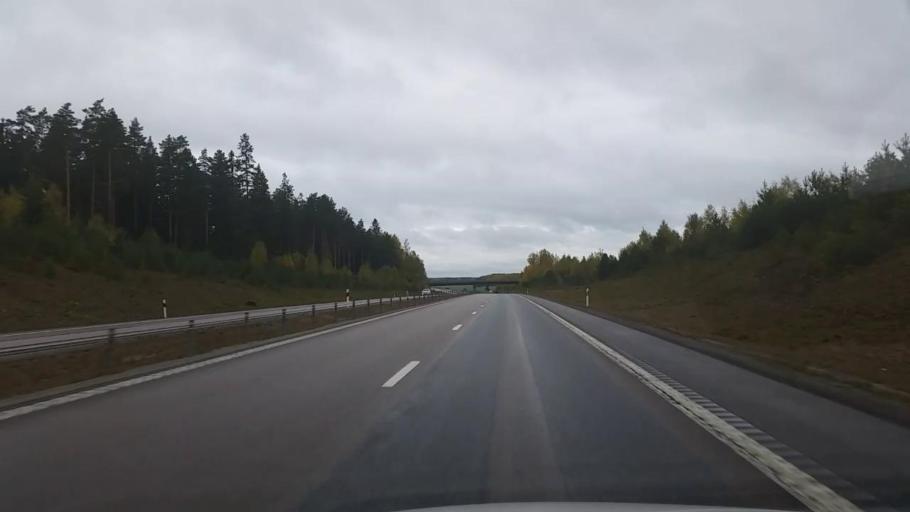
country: SE
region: Uppsala
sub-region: Osthammars Kommun
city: Bjorklinge
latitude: 60.1345
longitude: 17.5473
